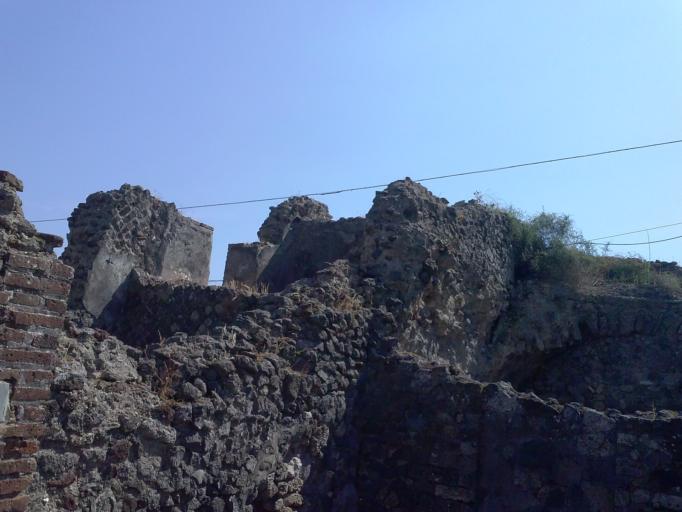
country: IT
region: Campania
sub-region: Provincia di Napoli
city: Pompei
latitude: 40.7506
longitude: 14.4828
